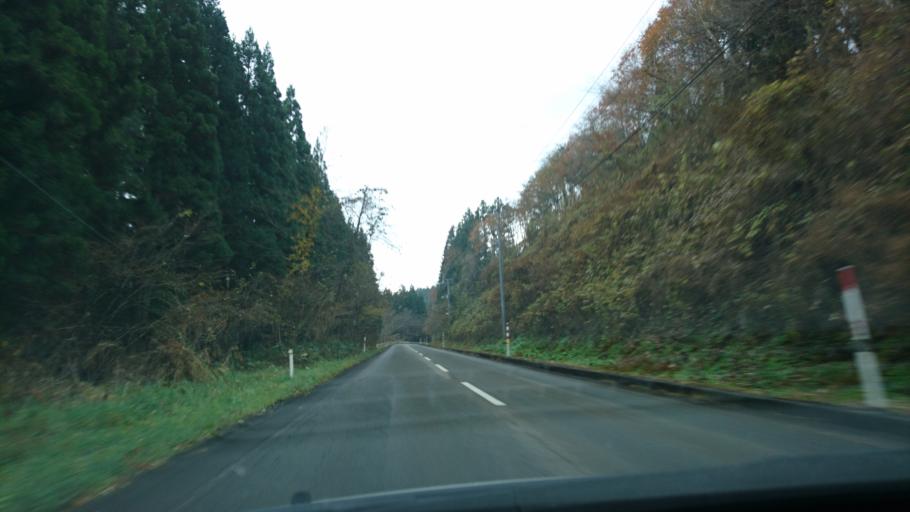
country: JP
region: Iwate
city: Ichinoseki
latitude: 38.9709
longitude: 140.9403
